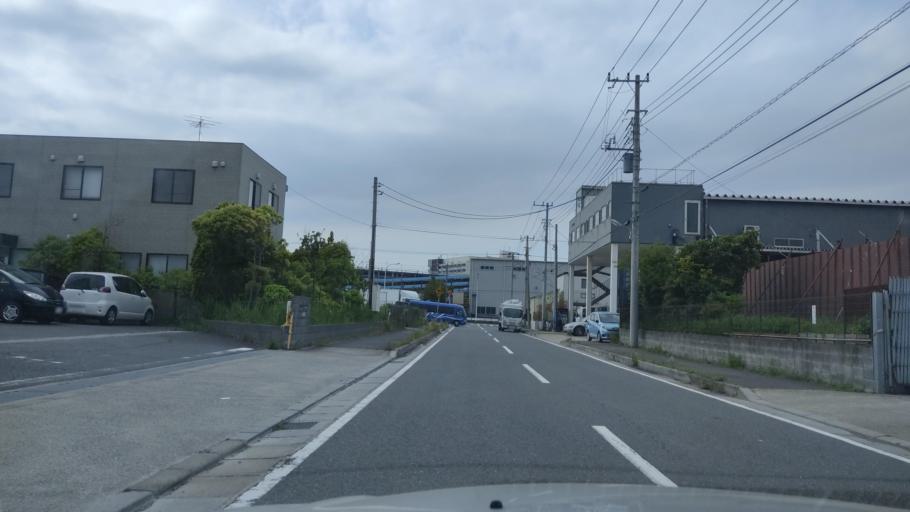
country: JP
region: Tokyo
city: Urayasu
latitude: 35.6226
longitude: 139.8971
